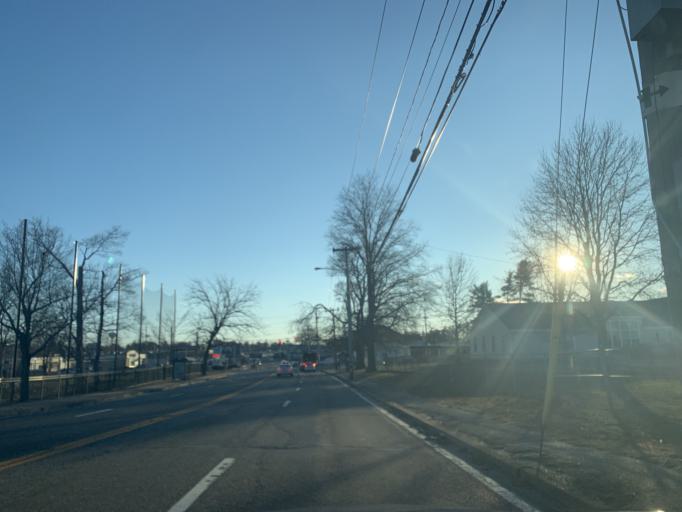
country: US
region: Rhode Island
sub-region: Providence County
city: East Providence
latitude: 41.8176
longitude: -71.3561
